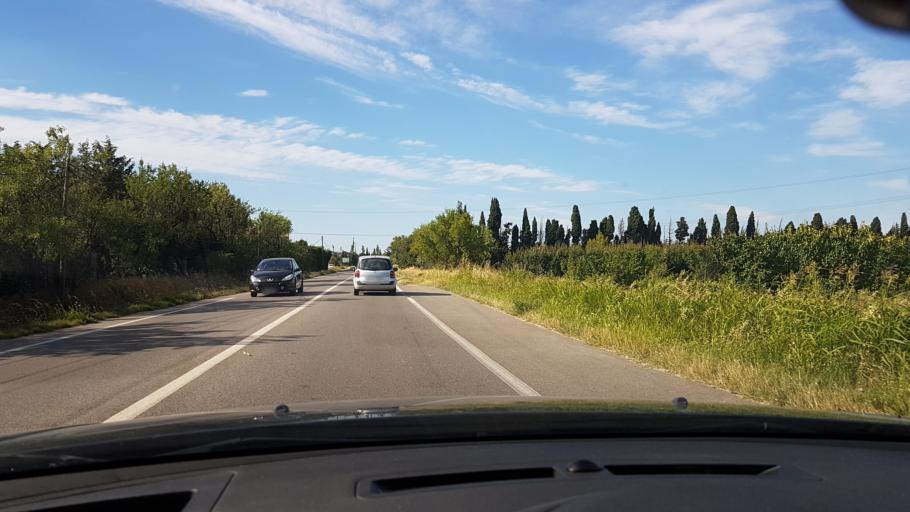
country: FR
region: Provence-Alpes-Cote d'Azur
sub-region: Departement des Bouches-du-Rhone
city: Graveson
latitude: 43.8613
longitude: 4.7691
